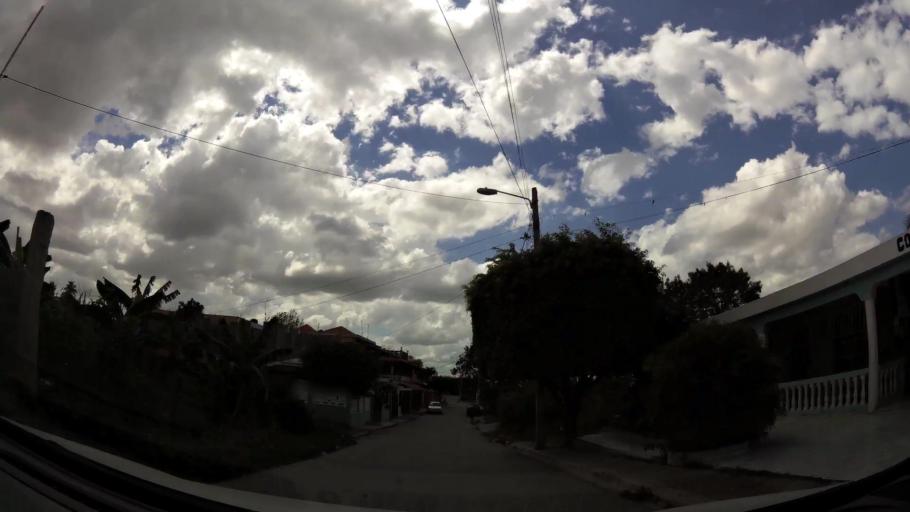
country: DO
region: Nacional
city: Ensanche Luperon
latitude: 18.5326
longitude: -69.9090
